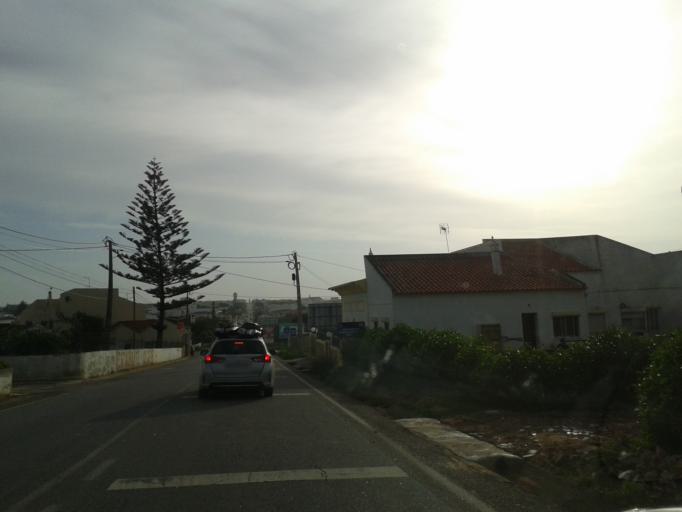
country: PT
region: Faro
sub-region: Vila do Bispo
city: Sagres
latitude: 37.0199
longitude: -8.9390
